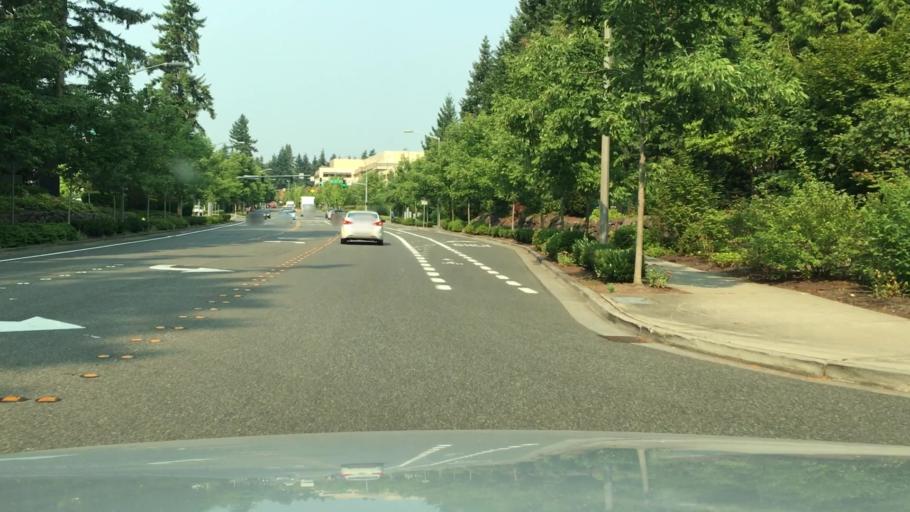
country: US
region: Washington
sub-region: King County
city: Redmond
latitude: 47.6408
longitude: -122.1375
